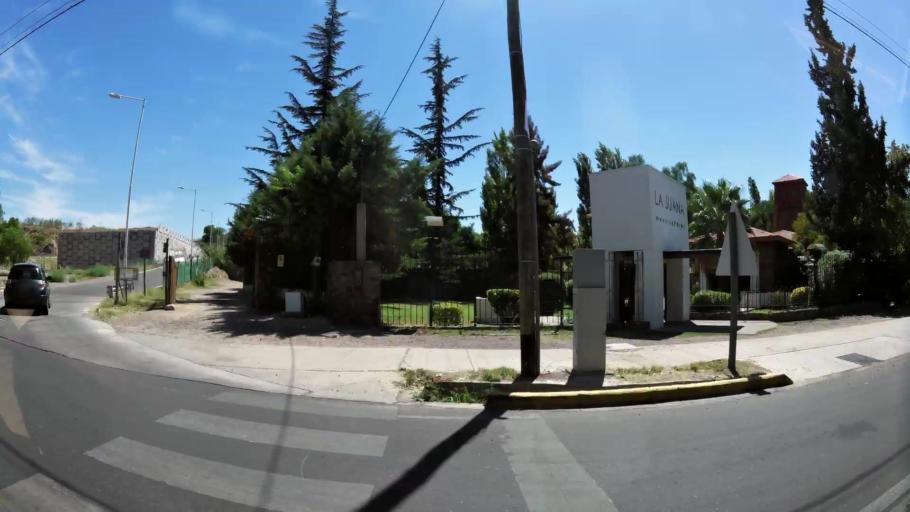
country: AR
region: Mendoza
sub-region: Departamento de Godoy Cruz
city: Godoy Cruz
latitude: -32.9600
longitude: -68.8642
